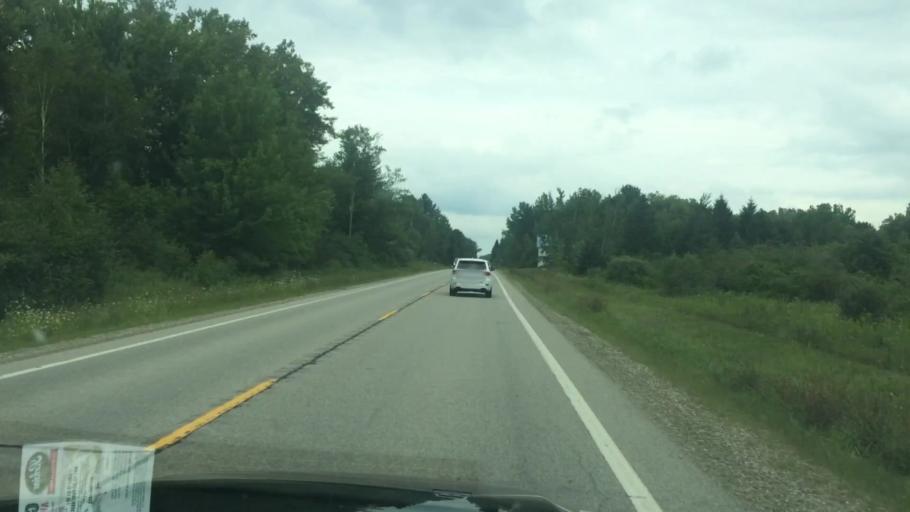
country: US
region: Michigan
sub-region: Tuscola County
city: Cass City
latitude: 43.4914
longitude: -83.0912
